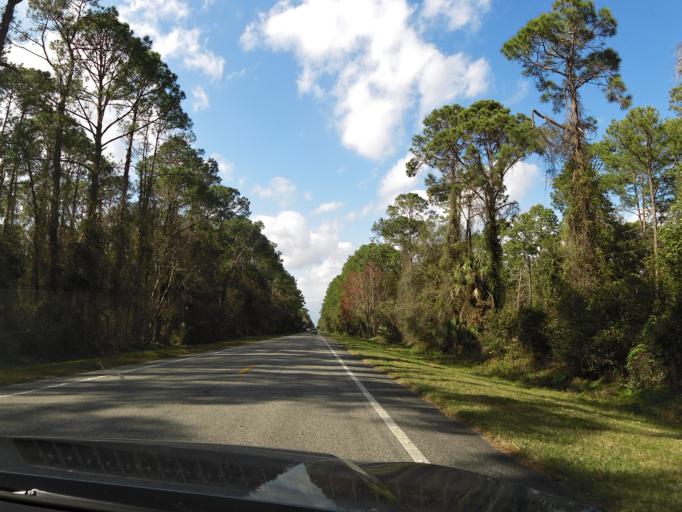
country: US
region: Florida
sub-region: Volusia County
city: De Leon Springs
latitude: 29.1456
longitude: -81.3679
